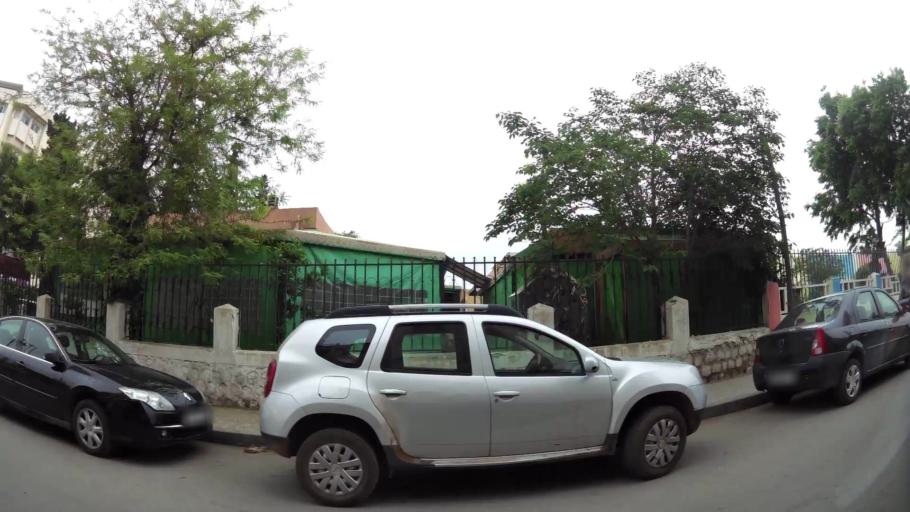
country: MA
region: Fes-Boulemane
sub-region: Fes
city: Fes
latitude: 34.0378
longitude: -4.9960
